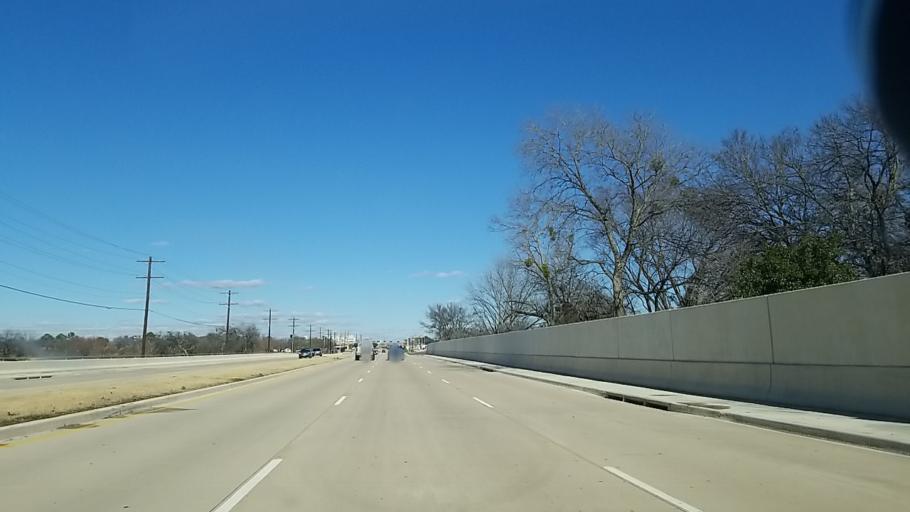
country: US
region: Texas
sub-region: Denton County
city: Corinth
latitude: 33.1660
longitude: -97.0909
